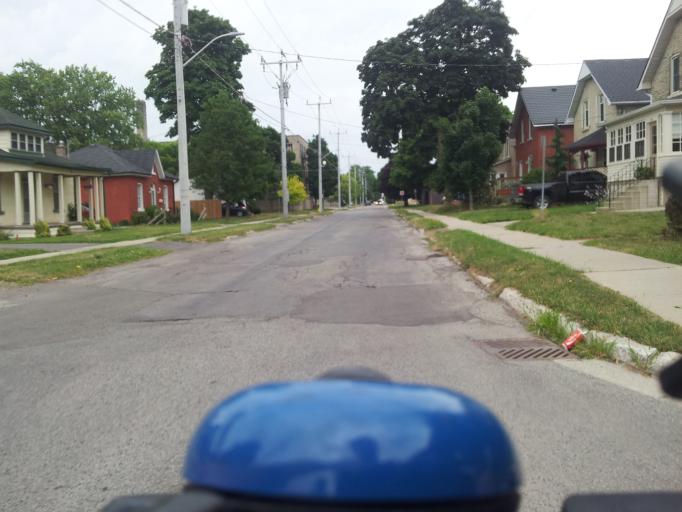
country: CA
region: Ontario
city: Stratford
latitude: 43.3695
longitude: -80.9677
